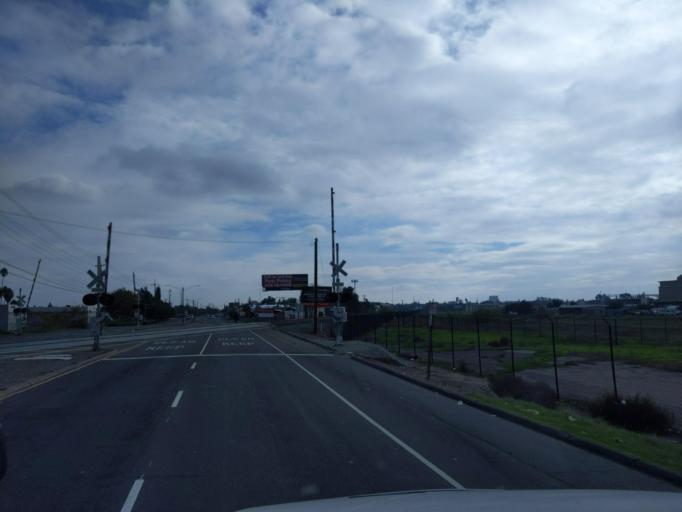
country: US
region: California
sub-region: San Joaquin County
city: August
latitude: 37.9813
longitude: -121.2829
